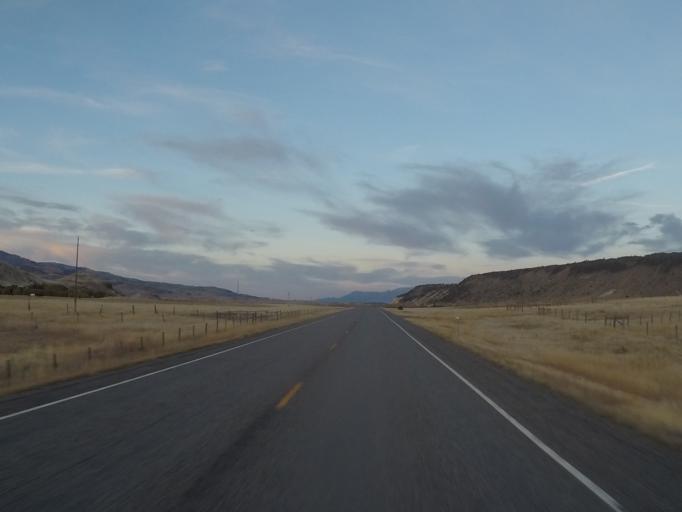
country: US
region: Montana
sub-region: Gallatin County
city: Bozeman
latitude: 45.2790
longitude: -110.8530
